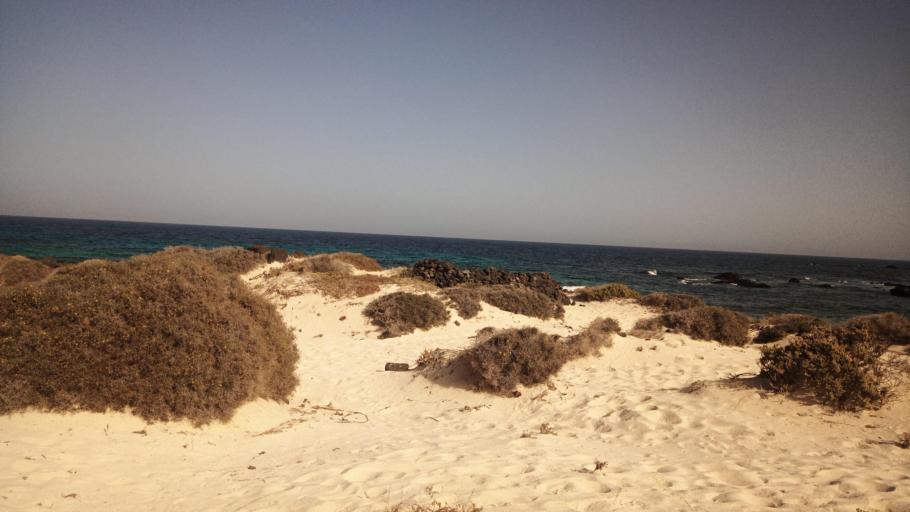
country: ES
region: Canary Islands
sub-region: Provincia de Las Palmas
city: Haria
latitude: 29.2060
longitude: -13.4247
